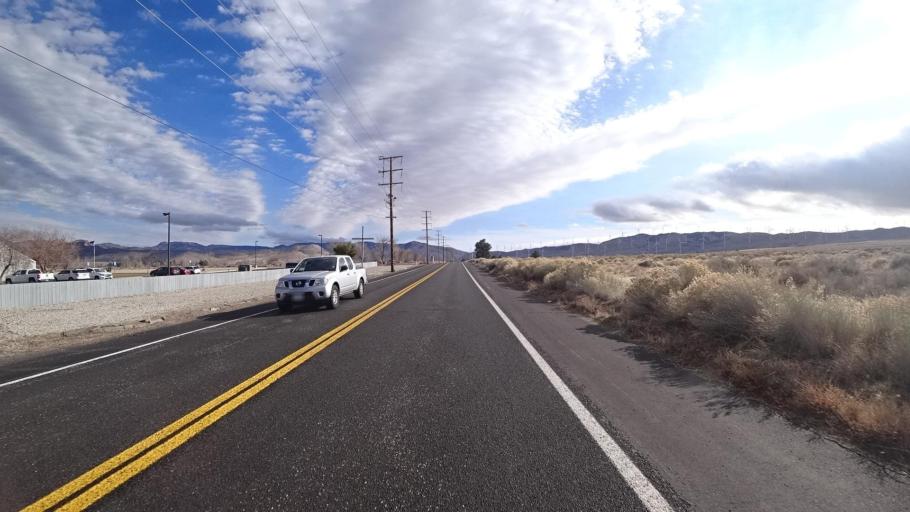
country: US
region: California
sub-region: Kern County
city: Tehachapi
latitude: 35.1098
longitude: -118.4092
